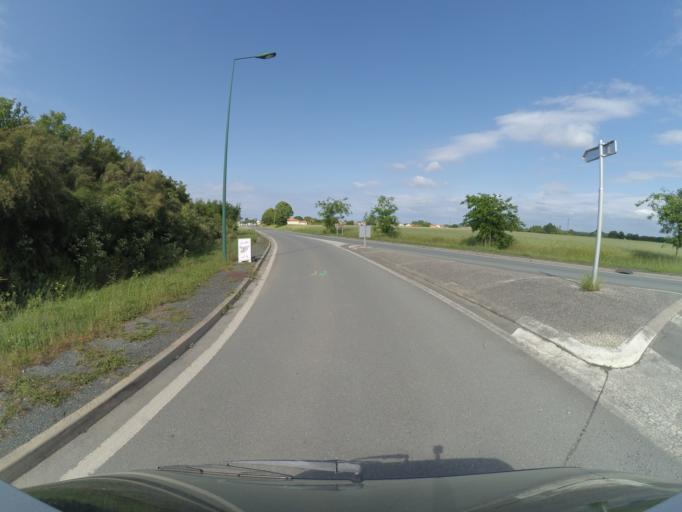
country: FR
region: Poitou-Charentes
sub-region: Departement de la Charente-Maritime
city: Saint-Xandre
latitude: 46.2347
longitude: -1.0736
